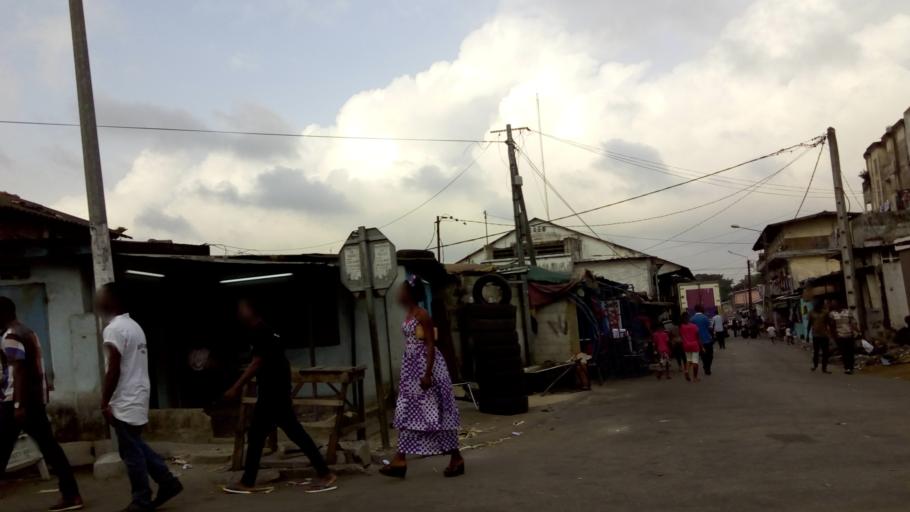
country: CI
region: Lagunes
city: Abidjan
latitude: 5.3392
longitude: -4.0262
